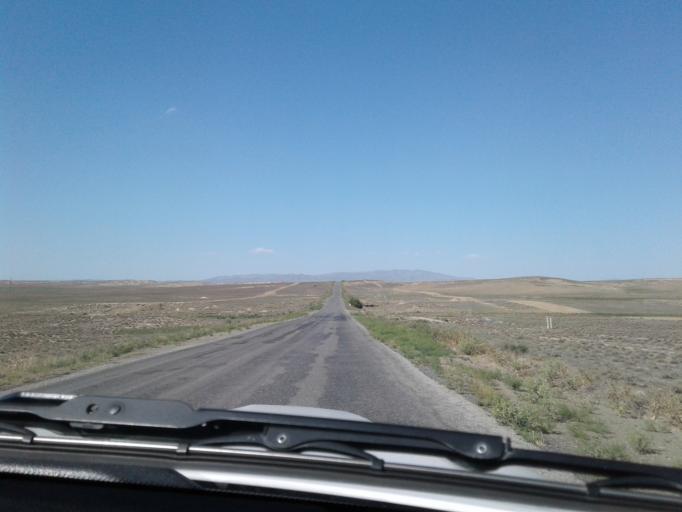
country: TM
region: Balkan
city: Magtymguly
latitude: 38.6295
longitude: 56.2399
